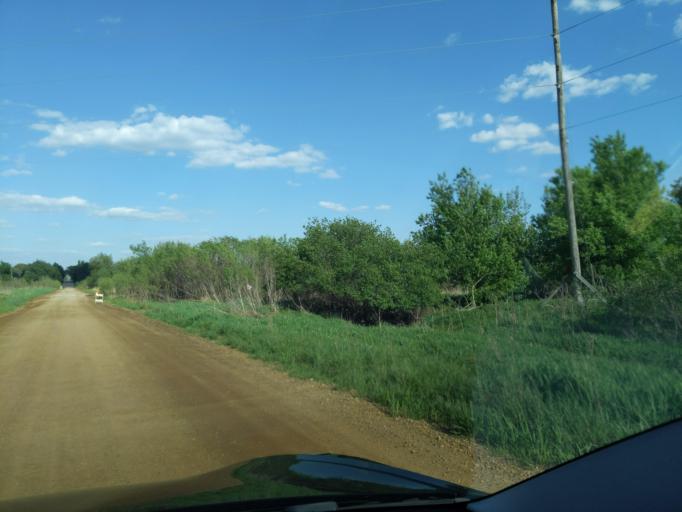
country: US
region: Michigan
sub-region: Eaton County
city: Potterville
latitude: 42.6828
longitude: -84.7254
